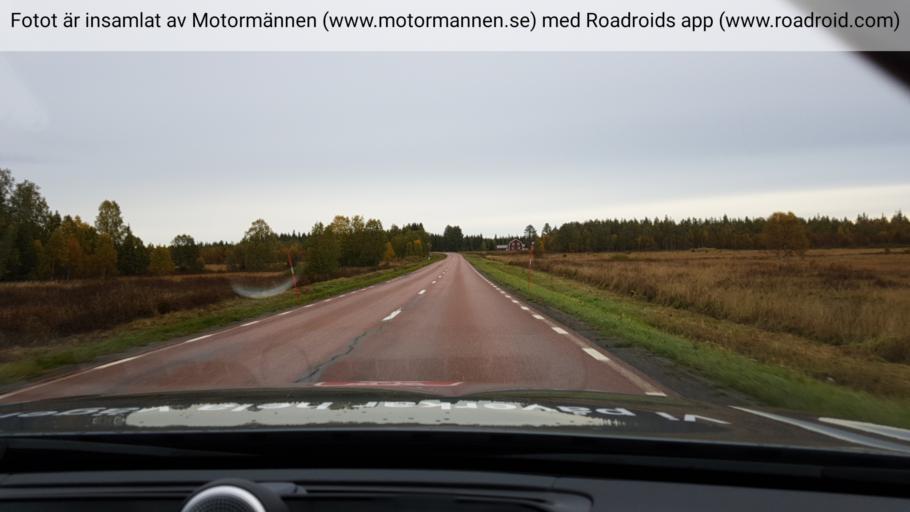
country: SE
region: Jaemtland
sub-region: Stroemsunds Kommun
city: Stroemsund
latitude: 63.7429
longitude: 15.4919
